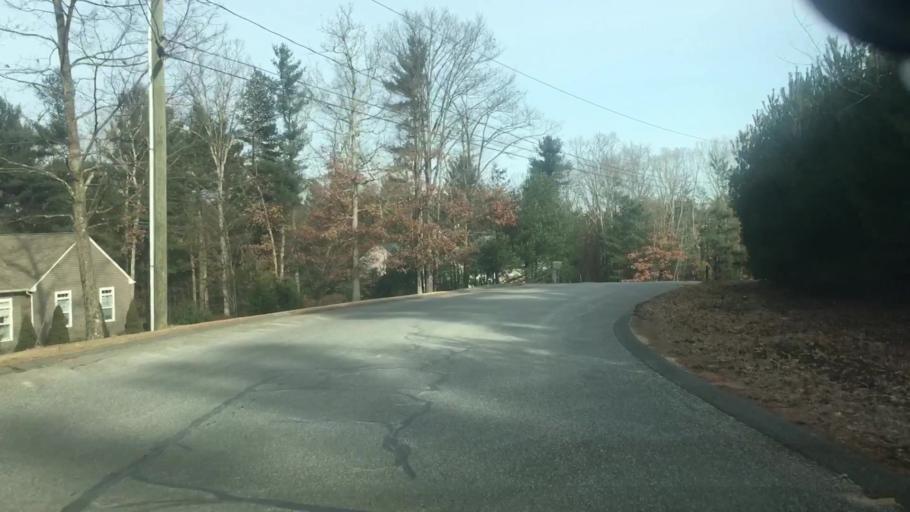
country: US
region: Connecticut
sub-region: Tolland County
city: Stafford
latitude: 41.9752
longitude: -72.3024
